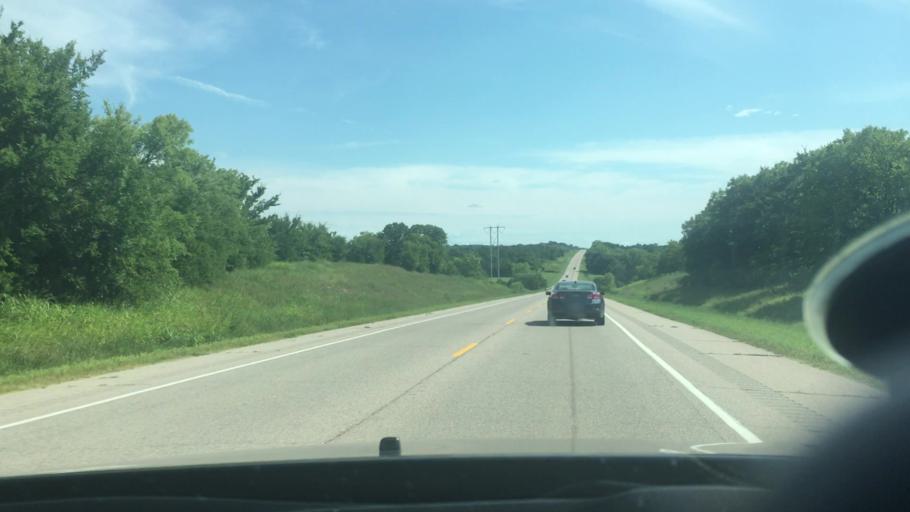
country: US
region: Oklahoma
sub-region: Seminole County
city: Konawa
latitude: 35.0323
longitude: -96.6783
